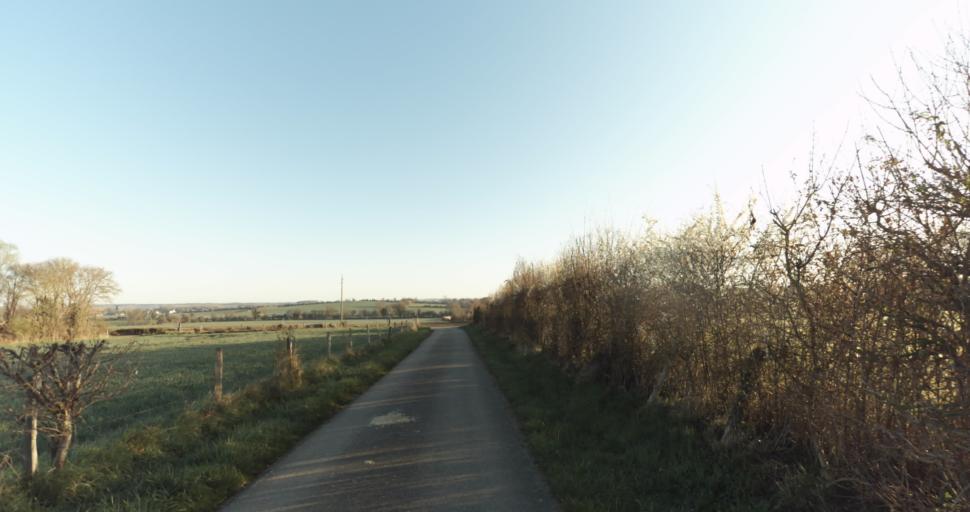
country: FR
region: Lower Normandy
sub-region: Departement du Calvados
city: Saint-Pierre-sur-Dives
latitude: 49.0259
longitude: -0.0170
